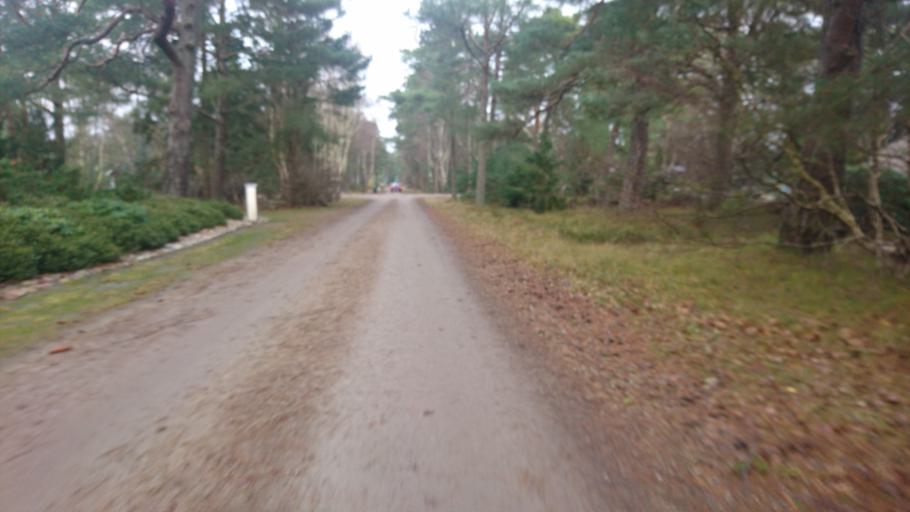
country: SE
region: Skane
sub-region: Vellinge Kommun
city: Ljunghusen
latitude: 55.3892
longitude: 12.9194
